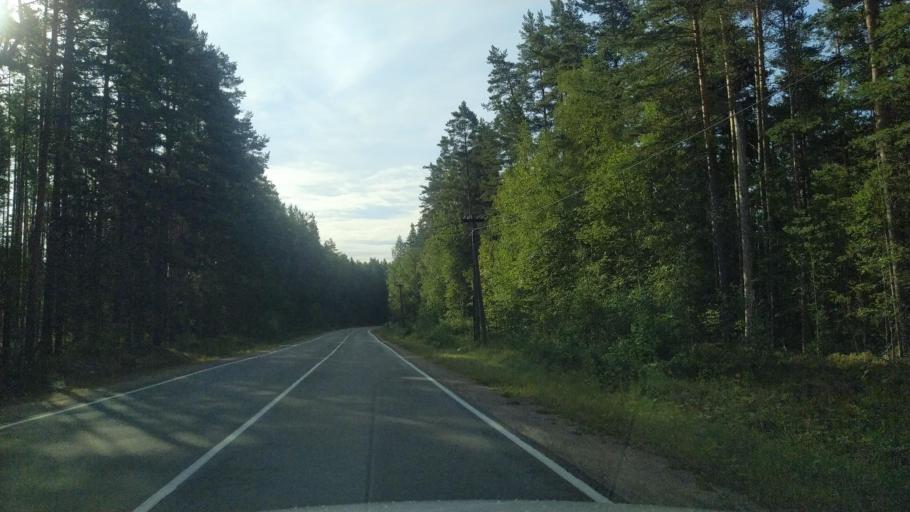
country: RU
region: Leningrad
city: Priozersk
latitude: 61.0020
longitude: 30.2377
